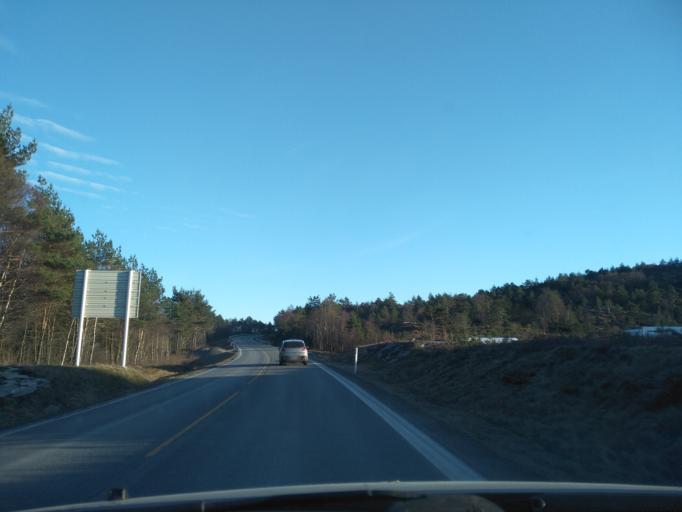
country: NO
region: Rogaland
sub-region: Tysvaer
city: Aksdal
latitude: 59.4063
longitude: 5.4604
